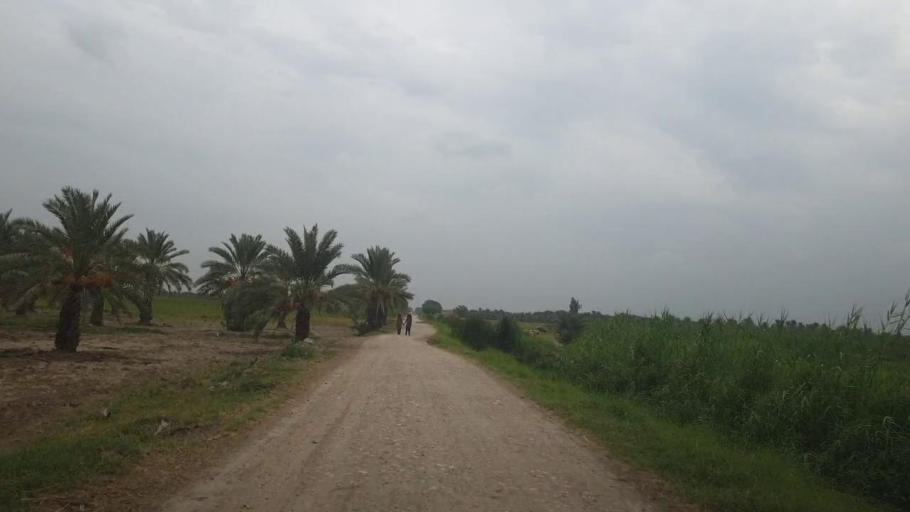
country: PK
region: Sindh
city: Khairpur
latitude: 27.5668
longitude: 68.7180
